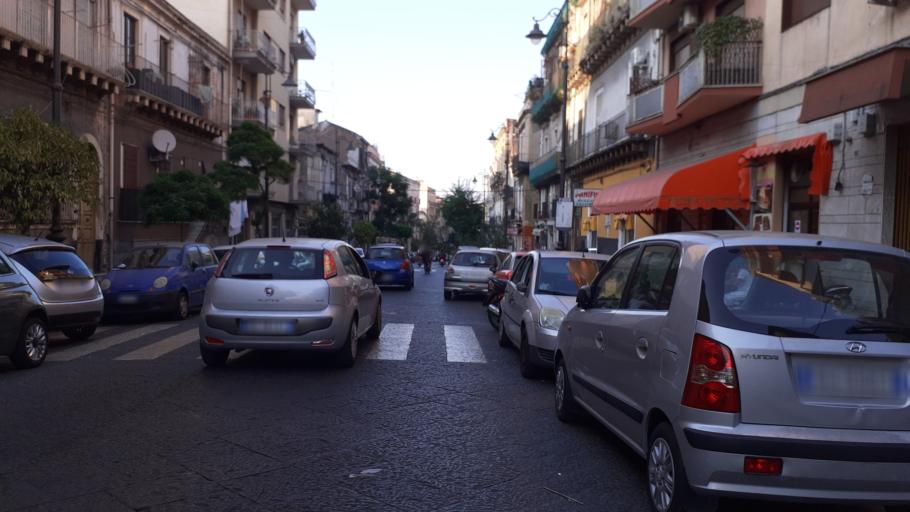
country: IT
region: Sicily
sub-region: Catania
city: Catania
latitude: 37.4983
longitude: 15.0857
